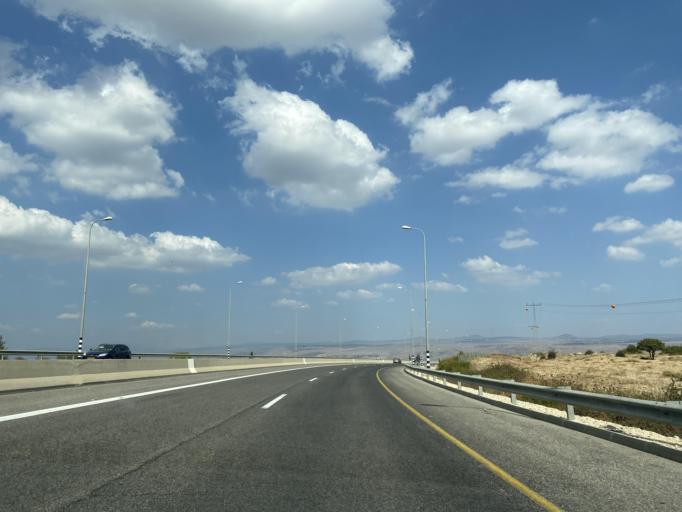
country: IL
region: Northern District
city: Rosh Pinna
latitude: 33.0267
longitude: 35.5579
